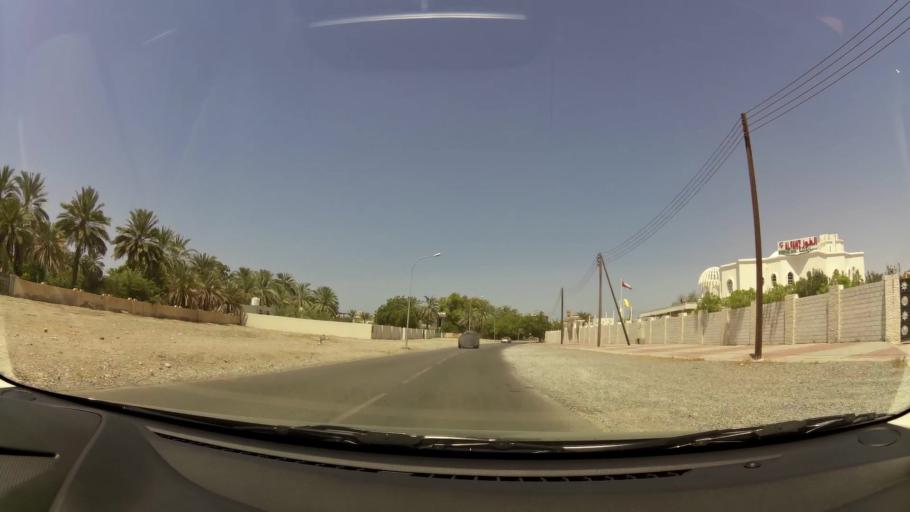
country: OM
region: Muhafazat Masqat
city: As Sib al Jadidah
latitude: 23.6174
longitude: 58.2276
